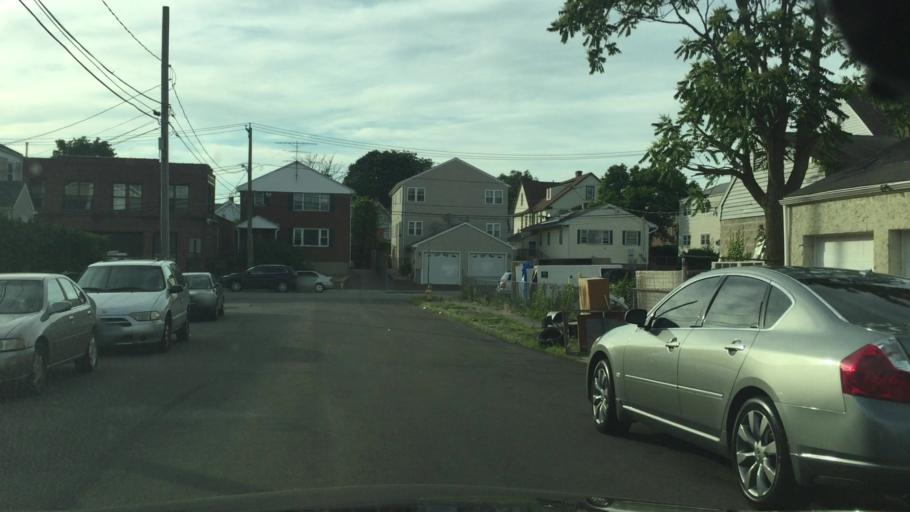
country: US
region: Connecticut
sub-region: Fairfield County
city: Bridgeport
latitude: 41.1910
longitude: -73.2059
